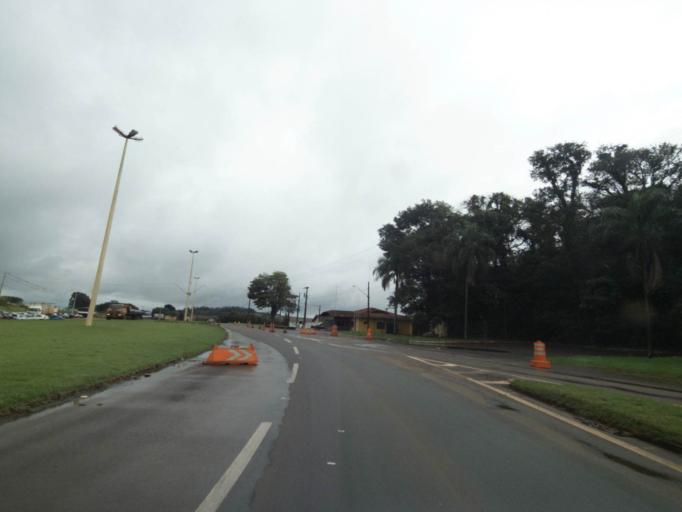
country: BR
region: Parana
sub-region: Marechal Candido Rondon
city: Marechal Candido Rondon
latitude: -24.5711
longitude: -53.9973
